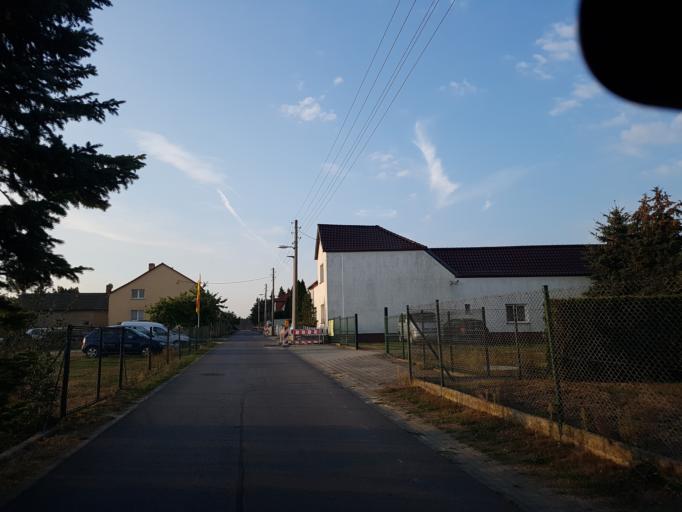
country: DE
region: Brandenburg
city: Plessa
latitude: 51.5335
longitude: 13.6373
